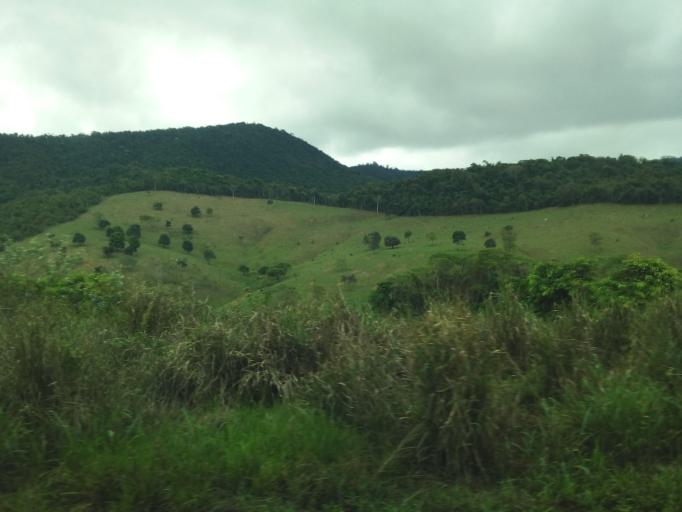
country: BR
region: Minas Gerais
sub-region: Nova Era
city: Nova Era
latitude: -19.6684
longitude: -42.8962
